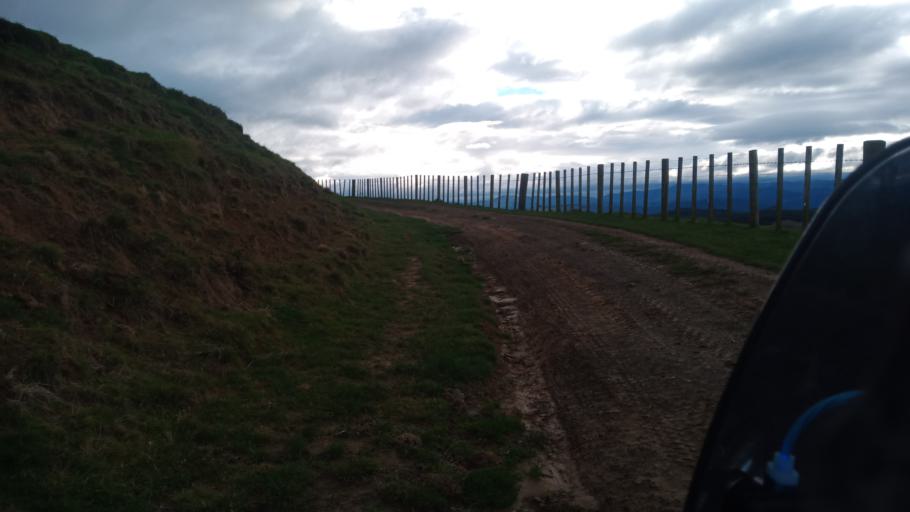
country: NZ
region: Gisborne
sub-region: Gisborne District
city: Gisborne
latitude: -38.3398
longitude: 177.9109
